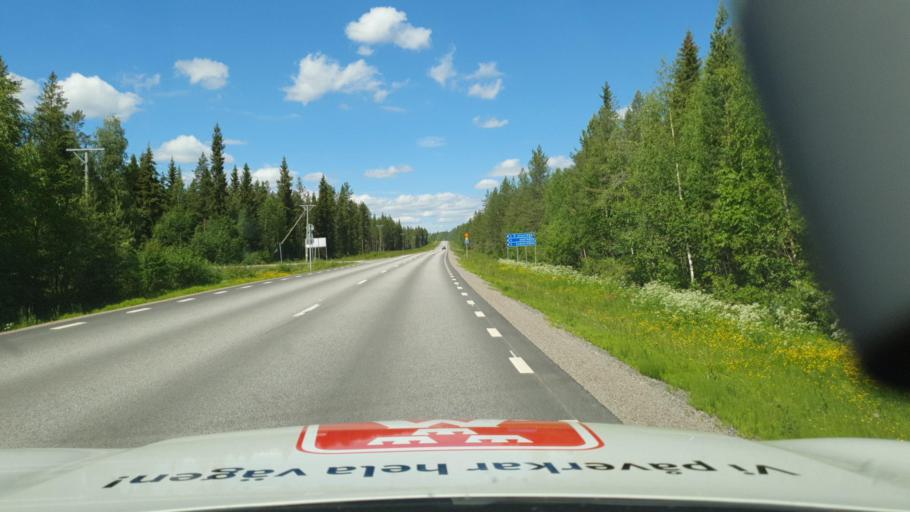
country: SE
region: Vaesterbotten
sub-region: Skelleftea Kommun
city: Langsele
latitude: 64.9467
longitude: 20.2710
